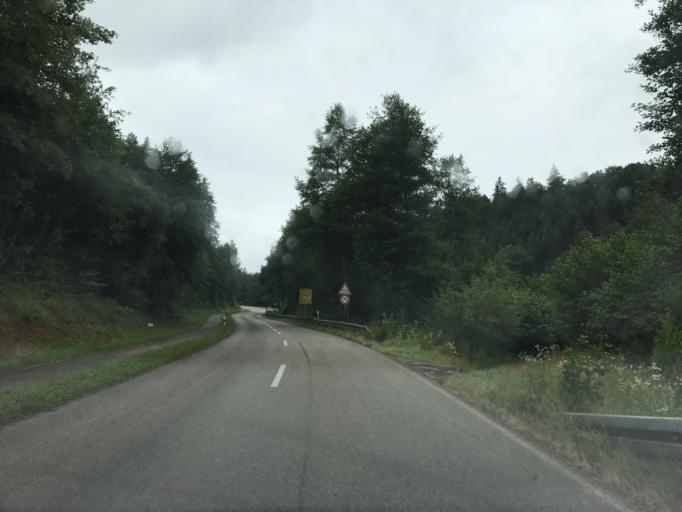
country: DE
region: Baden-Wuerttemberg
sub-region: Freiburg Region
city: Steinen
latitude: 47.6586
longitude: 7.7452
